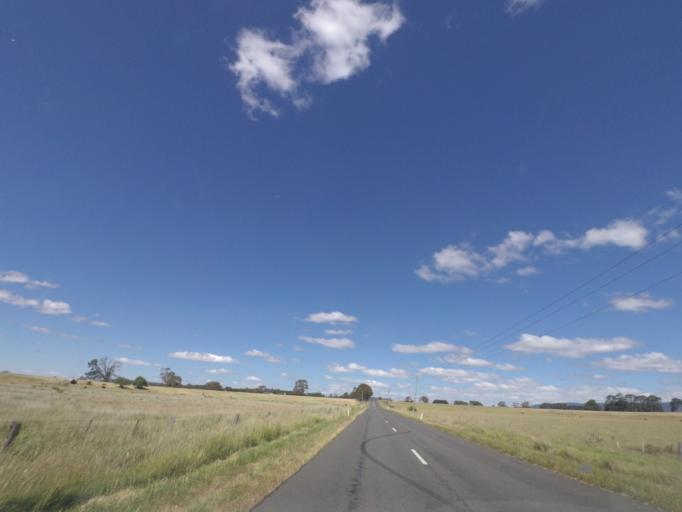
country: AU
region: Victoria
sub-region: Mount Alexander
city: Castlemaine
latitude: -37.2904
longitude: 144.4813
